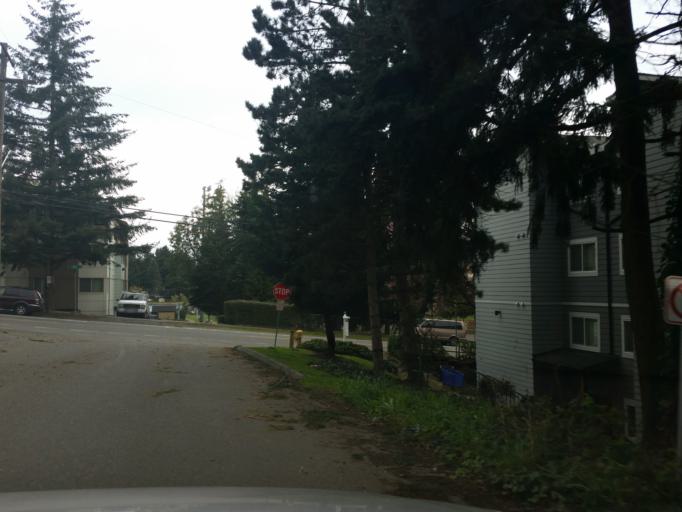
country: US
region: Washington
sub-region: King County
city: Shoreline
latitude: 47.7228
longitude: -122.3504
